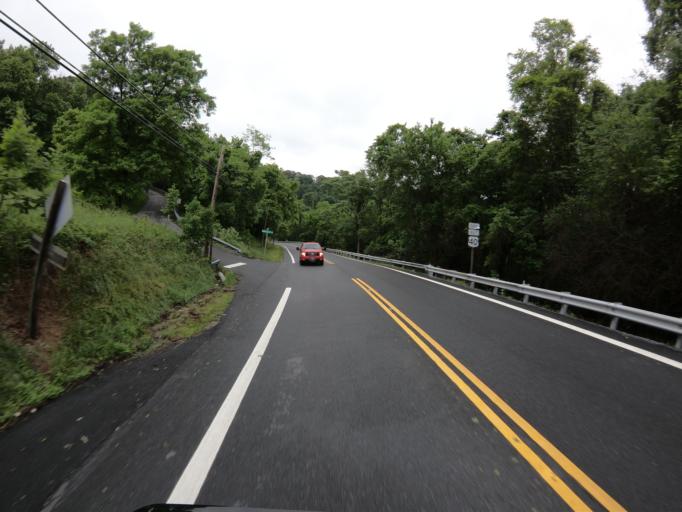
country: US
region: Maryland
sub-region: Washington County
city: Boonsboro
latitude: 39.4840
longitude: -77.6185
